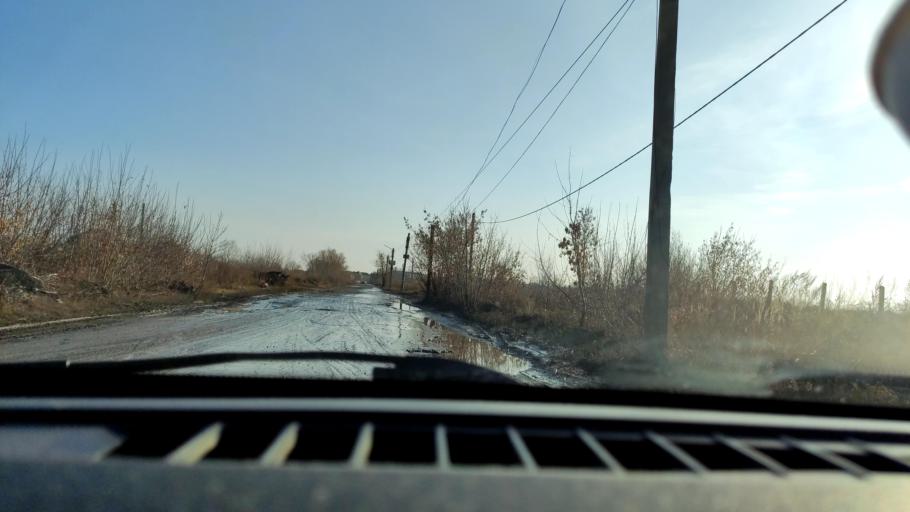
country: RU
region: Samara
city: Samara
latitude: 53.1189
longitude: 50.1051
